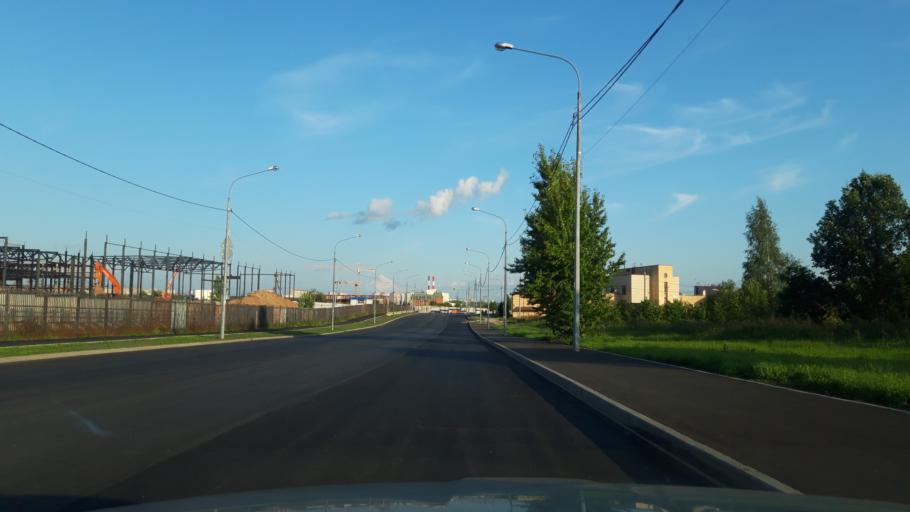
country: RU
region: Moskovskaya
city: Alabushevo
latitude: 56.0112
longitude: 37.1396
